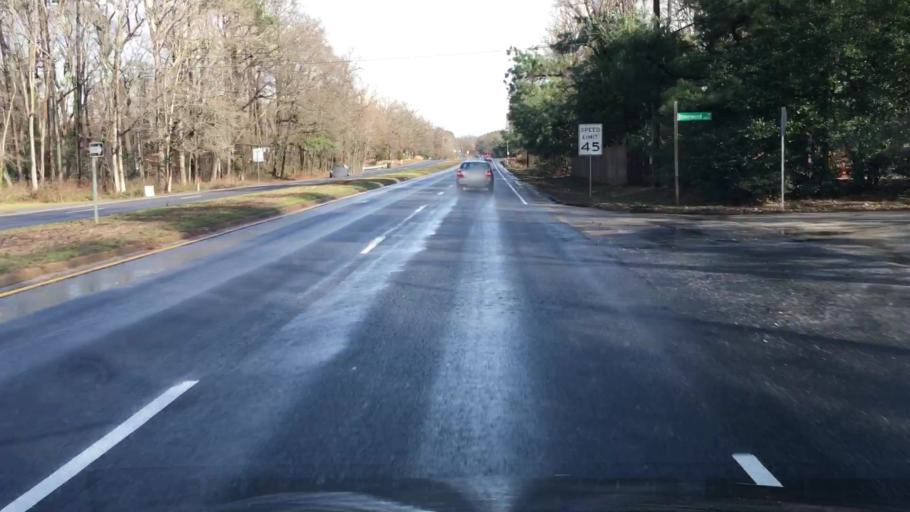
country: US
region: Virginia
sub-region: Chesterfield County
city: Bon Air
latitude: 37.5325
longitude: -77.5767
